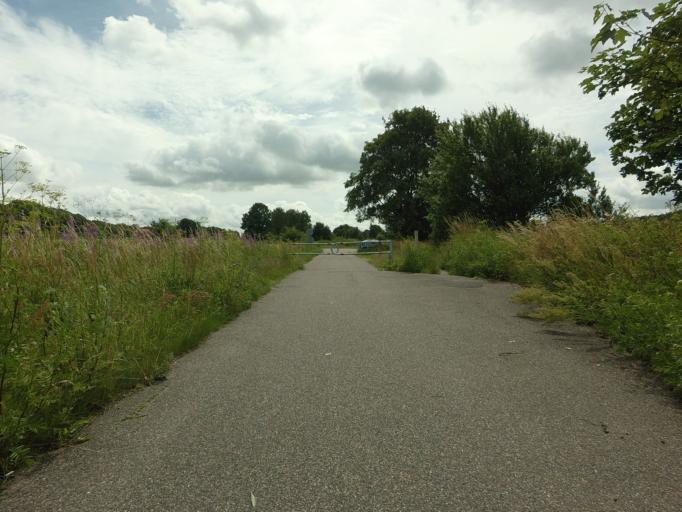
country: DK
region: Central Jutland
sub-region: Randers Kommune
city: Langa
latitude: 56.3670
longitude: 9.9015
